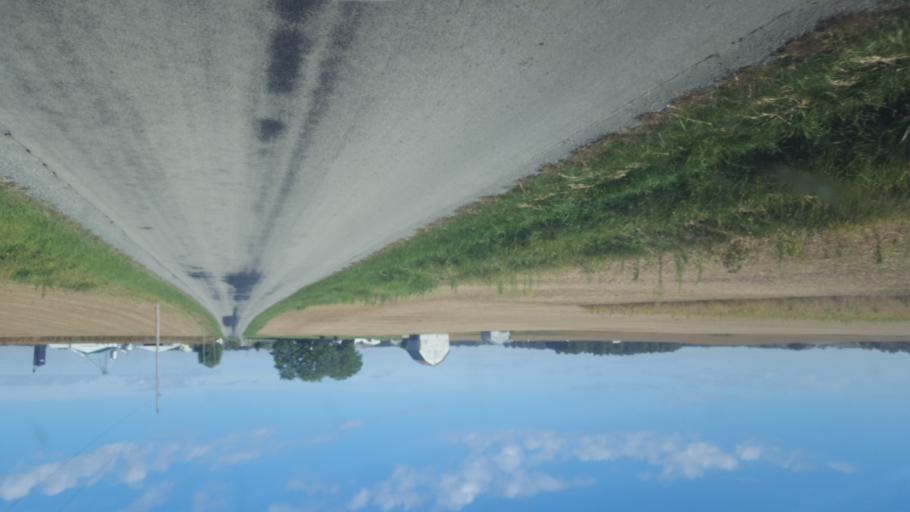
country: US
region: Ohio
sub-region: Wyandot County
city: Upper Sandusky
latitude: 40.8038
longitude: -83.2242
